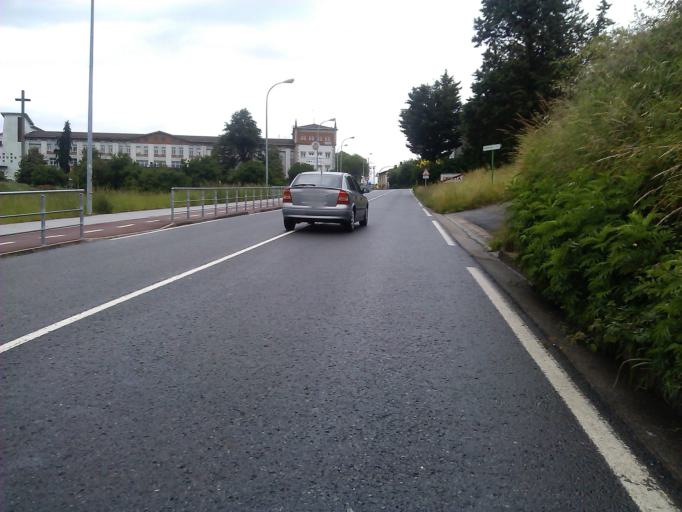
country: ES
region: Basque Country
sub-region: Provincia de Guipuzcoa
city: Urnieta
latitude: 43.2438
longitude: -1.9941
